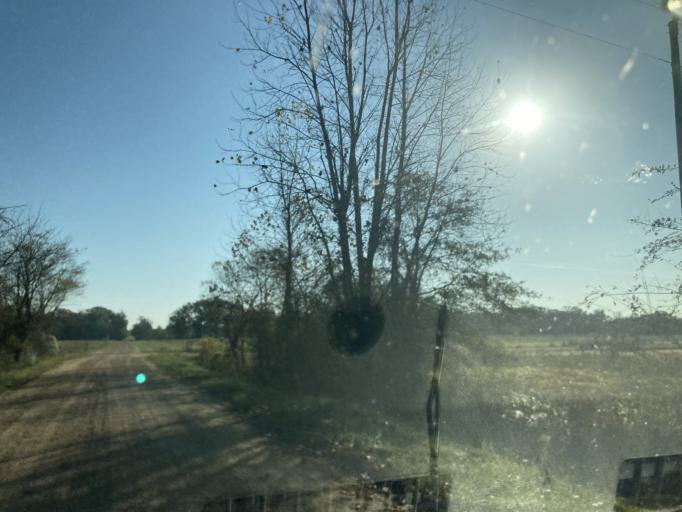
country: US
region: Mississippi
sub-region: Madison County
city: Kearney Park
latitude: 32.7058
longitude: -90.2506
